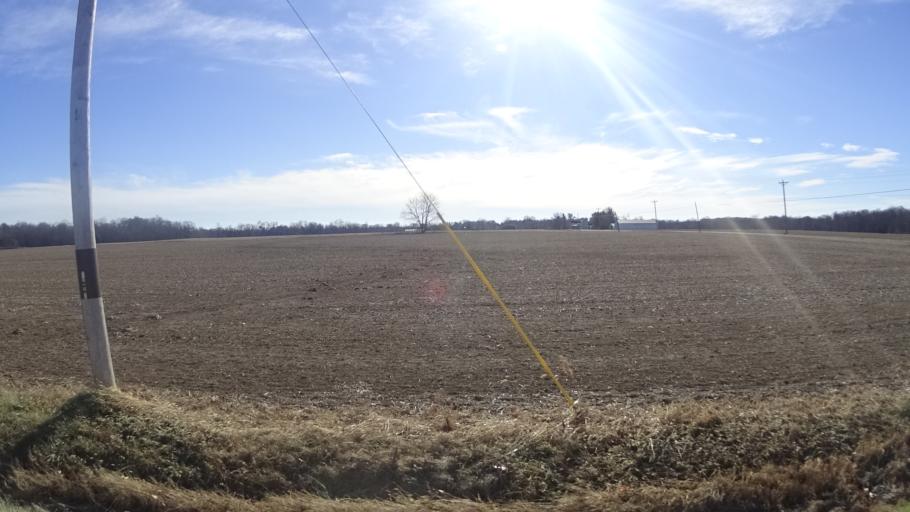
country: US
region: Ohio
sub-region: Lorain County
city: Camden
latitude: 41.2874
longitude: -82.3158
